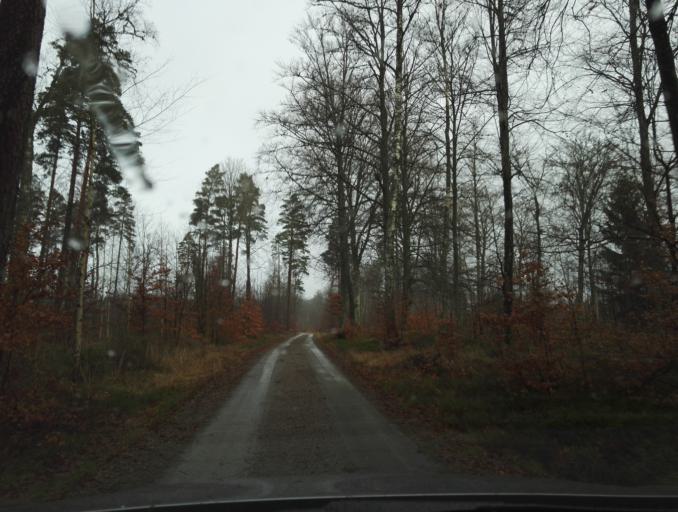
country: SE
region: Kronoberg
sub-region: Vaxjo Kommun
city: Vaexjoe
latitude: 56.9555
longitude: 14.7839
